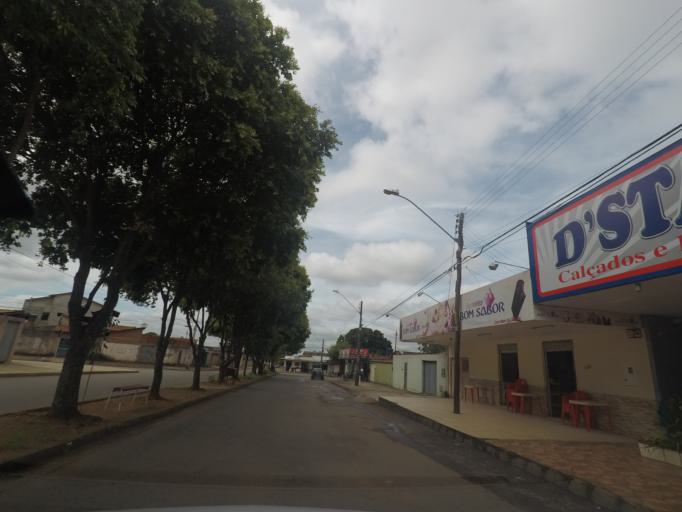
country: BR
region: Goias
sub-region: Goiania
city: Goiania
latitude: -16.6629
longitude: -49.1855
